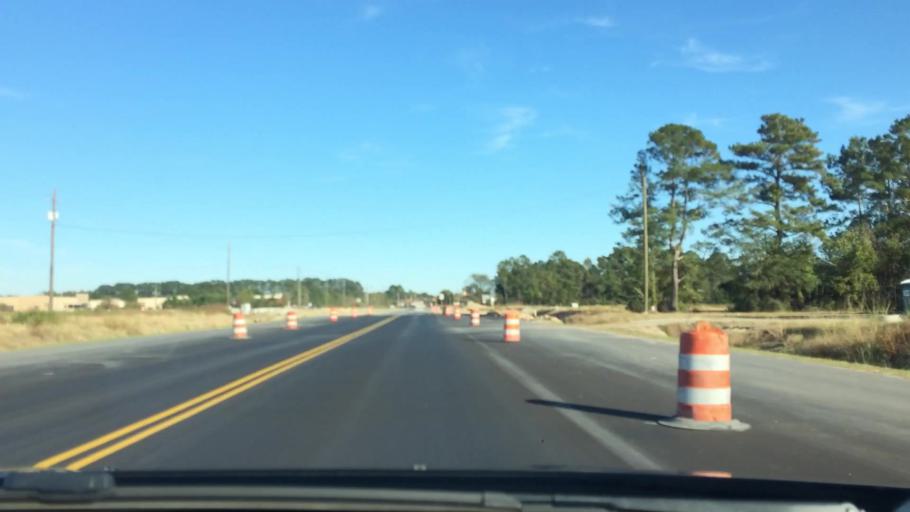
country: US
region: North Carolina
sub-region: Pitt County
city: Ayden
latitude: 35.4761
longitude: -77.4418
